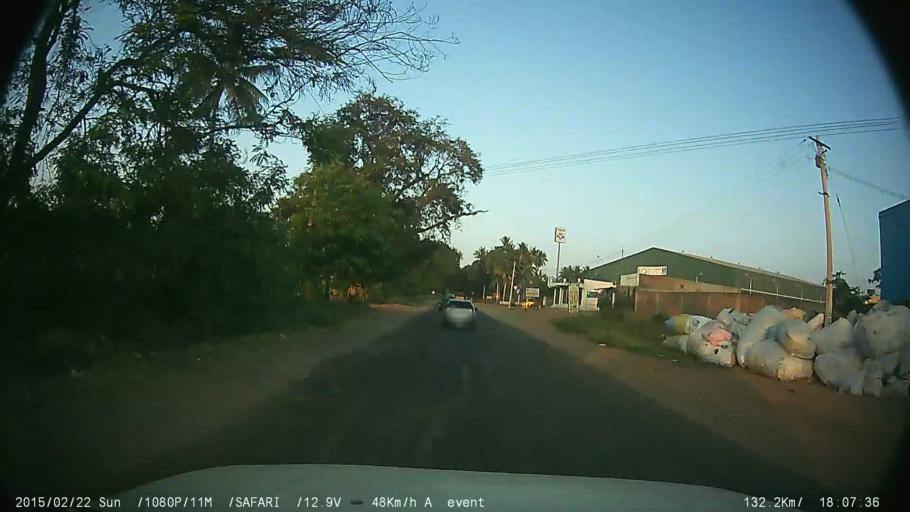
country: IN
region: Tamil Nadu
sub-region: Theni
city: Chinnamanur
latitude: 9.8340
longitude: 77.3759
